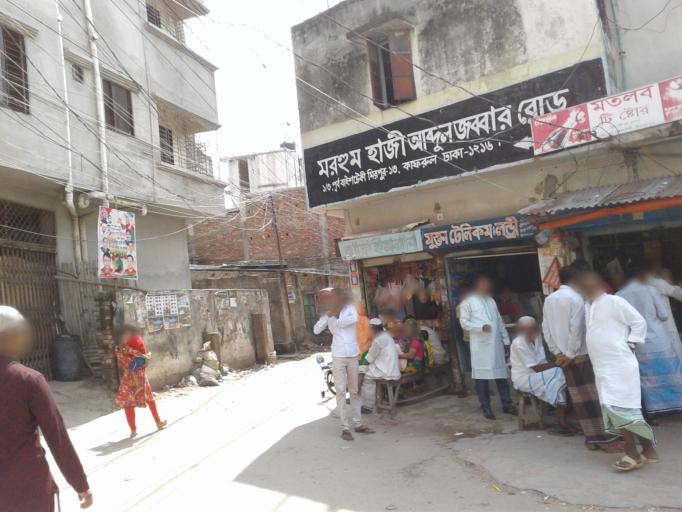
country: BD
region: Dhaka
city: Azimpur
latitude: 23.8093
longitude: 90.3792
